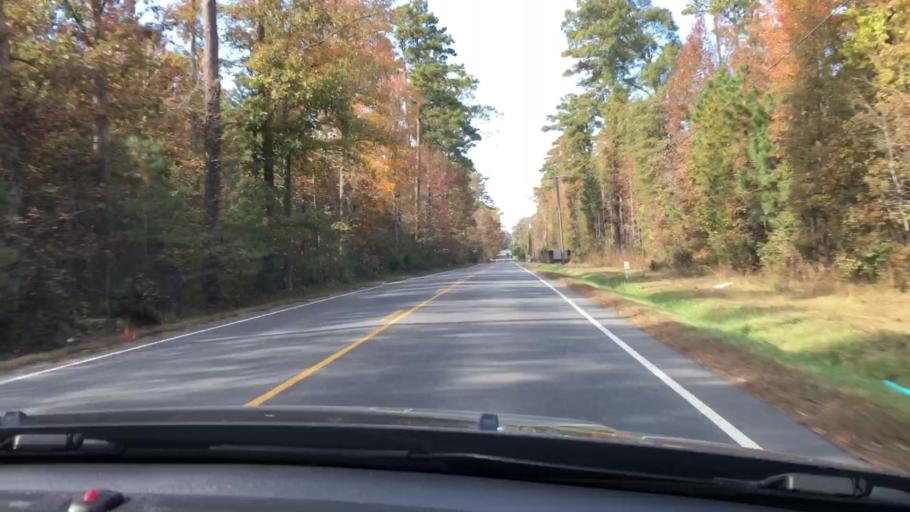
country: US
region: Virginia
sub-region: King William County
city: West Point
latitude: 37.5668
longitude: -76.8307
